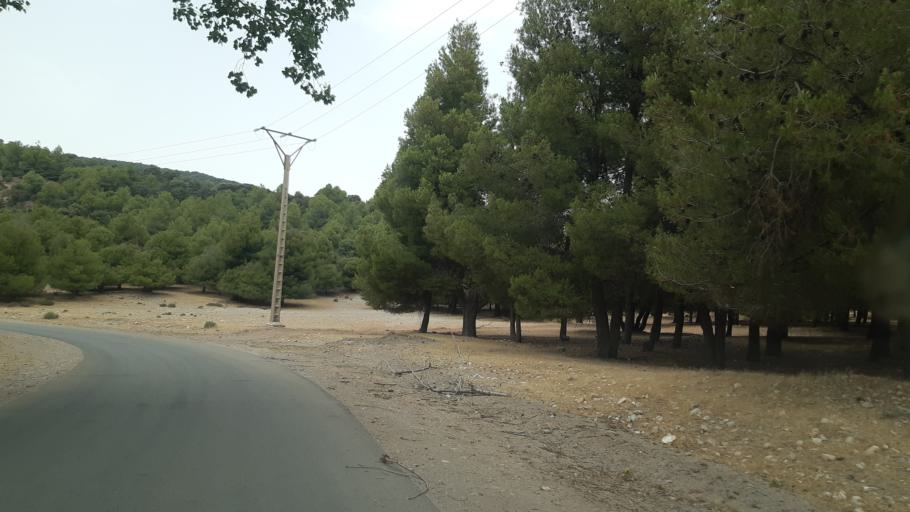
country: MA
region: Meknes-Tafilalet
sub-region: Ifrane
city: Ifrane
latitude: 33.6538
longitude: -5.0292
